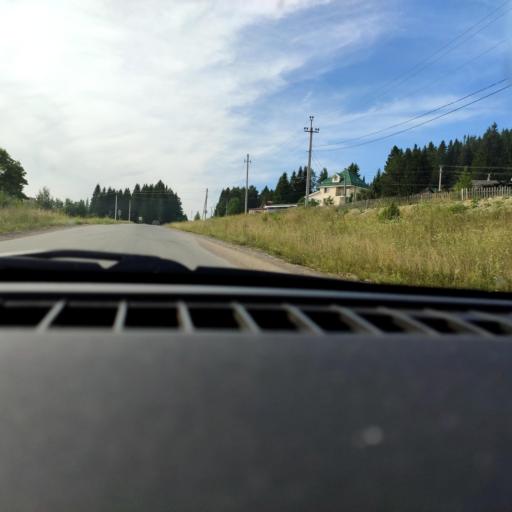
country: RU
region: Perm
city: Polazna
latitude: 58.3494
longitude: 56.2500
